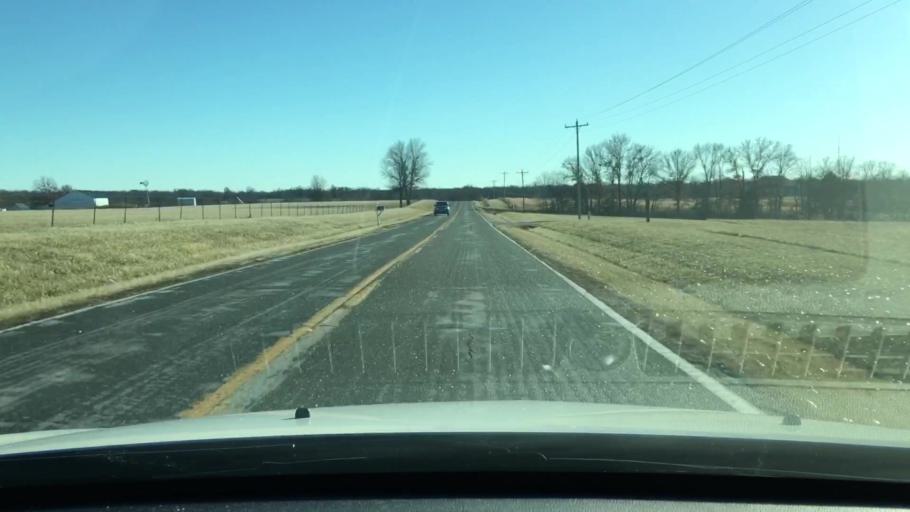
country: US
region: Missouri
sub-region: Audrain County
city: Mexico
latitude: 39.2648
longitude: -91.8288
